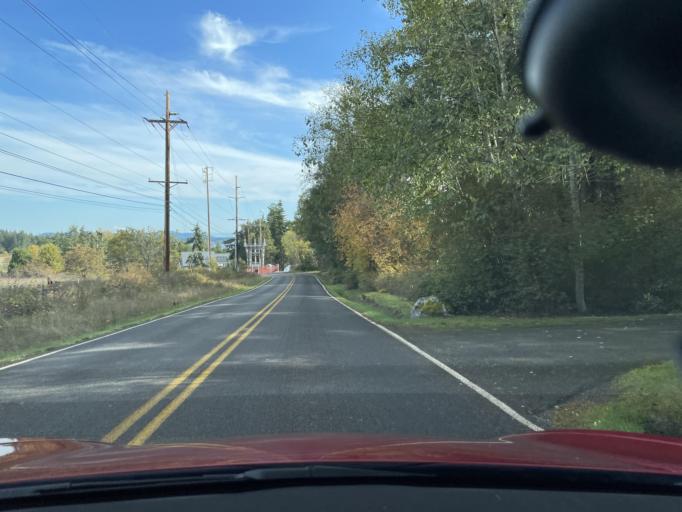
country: US
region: Washington
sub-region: San Juan County
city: Friday Harbor
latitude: 48.5181
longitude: -122.9837
